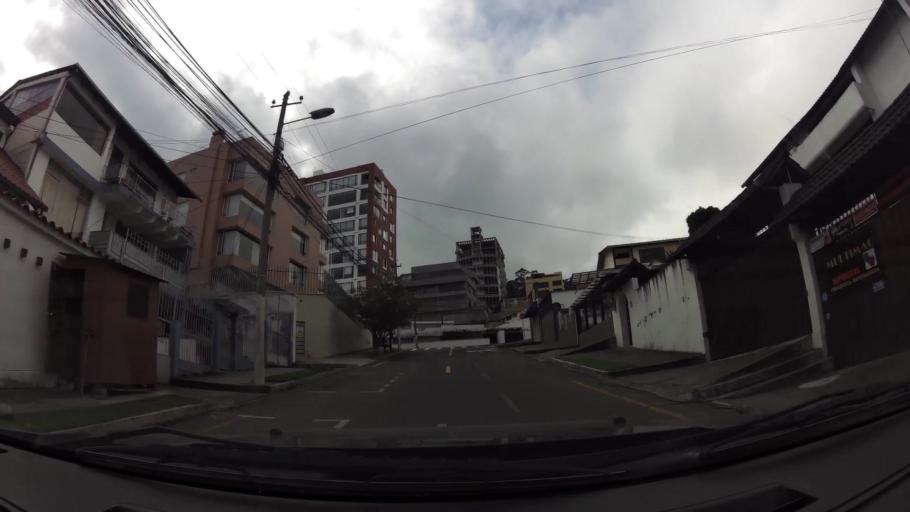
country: EC
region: Pichincha
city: Quito
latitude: -0.1800
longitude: -78.4755
